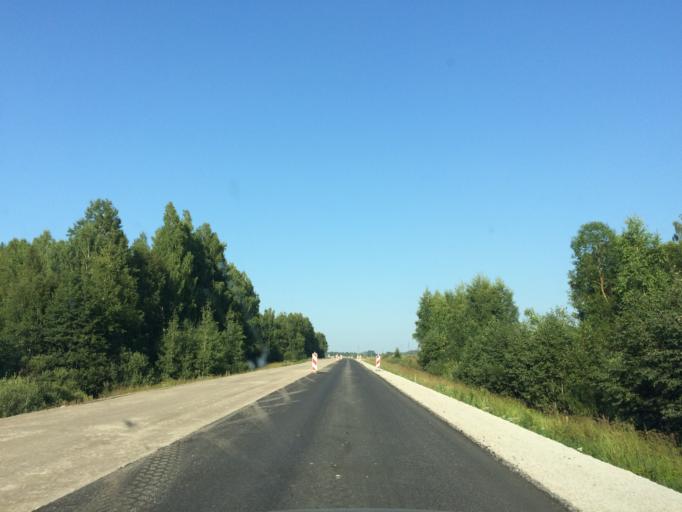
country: LV
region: Rezekne
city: Rezekne
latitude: 56.5164
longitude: 27.4953
